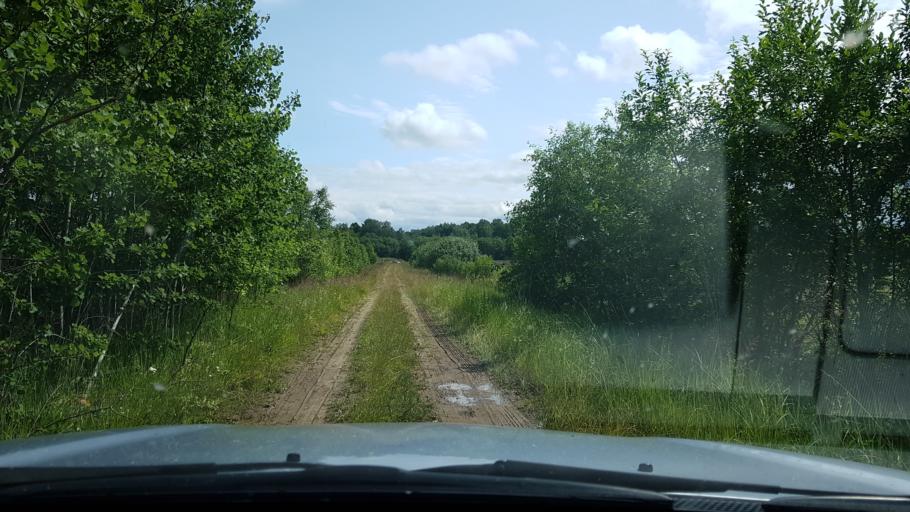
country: EE
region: Ida-Virumaa
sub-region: Sillamaee linn
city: Sillamae
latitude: 59.3646
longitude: 27.8096
